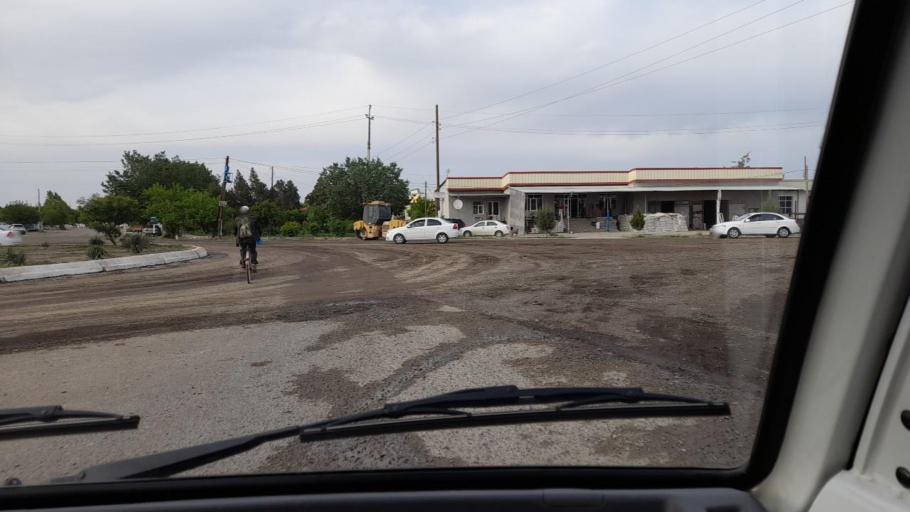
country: UZ
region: Bukhara
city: Romiton
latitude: 40.0455
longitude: 64.3290
